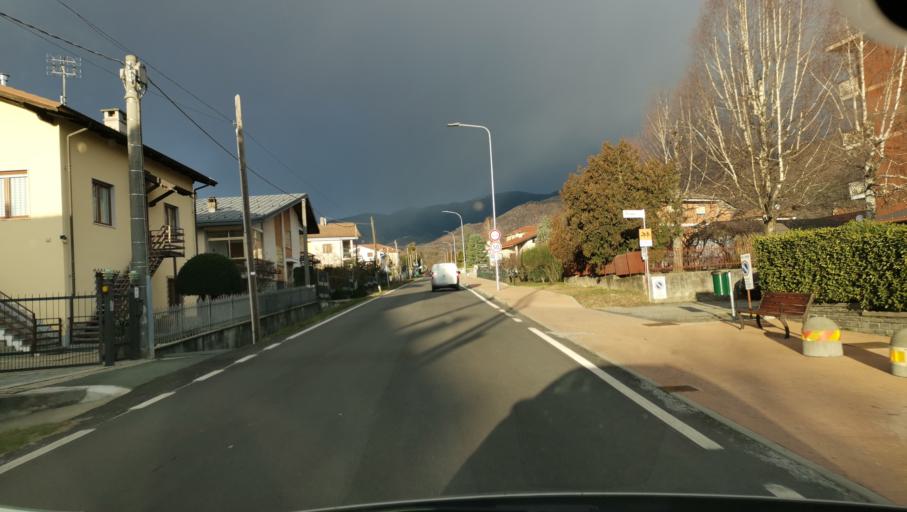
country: IT
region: Piedmont
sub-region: Provincia di Torino
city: Giaveno
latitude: 45.0462
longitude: 7.3457
